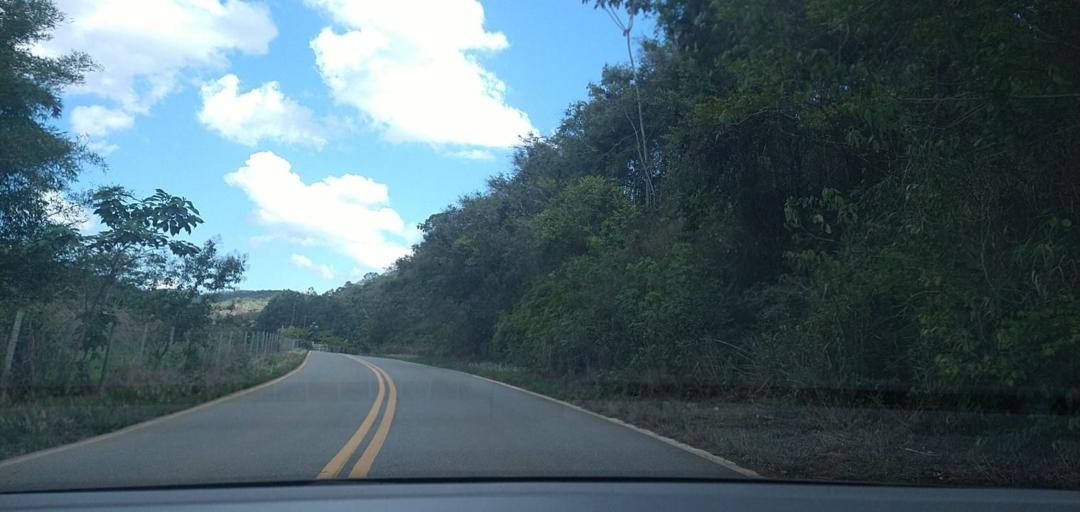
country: BR
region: Minas Gerais
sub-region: Rio Piracicaba
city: Rio Piracicaba
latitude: -19.9989
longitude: -43.1079
